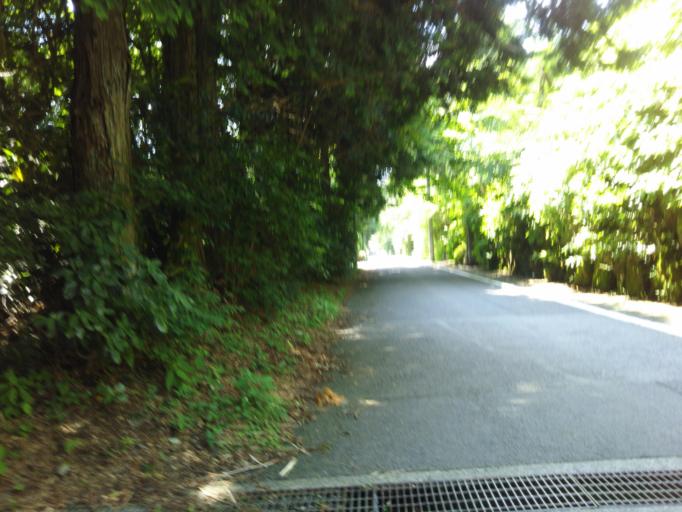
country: JP
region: Shizuoka
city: Gotemba
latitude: 35.2582
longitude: 138.9990
